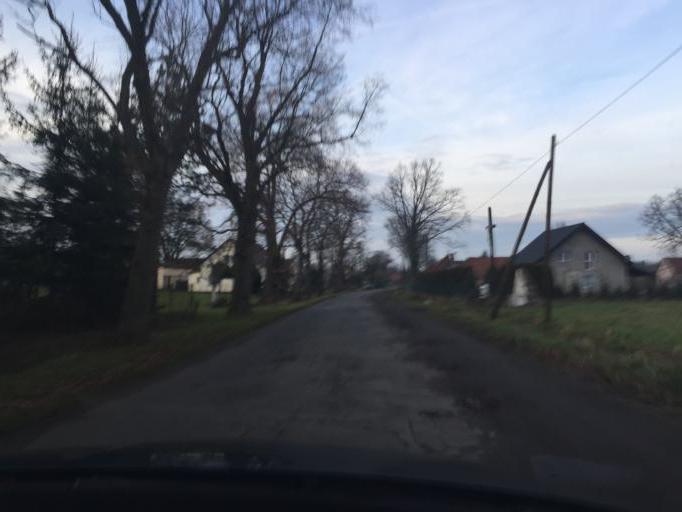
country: PL
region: Lubusz
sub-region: Powiat zielonogorski
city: Ochla
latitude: 51.8035
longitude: 15.4925
